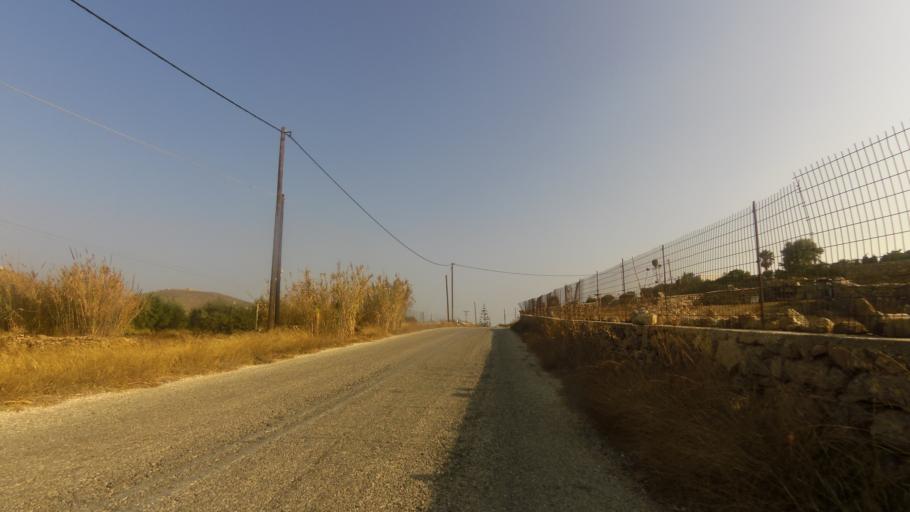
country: GR
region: South Aegean
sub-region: Nomos Kykladon
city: Antiparos
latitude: 37.0317
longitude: 25.0751
